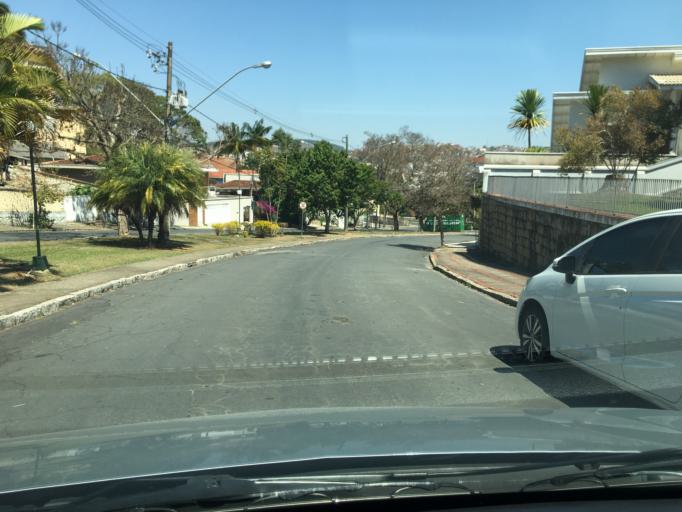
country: BR
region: Minas Gerais
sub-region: Pocos De Caldas
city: Pocos de Caldas
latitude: -21.7805
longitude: -46.5585
